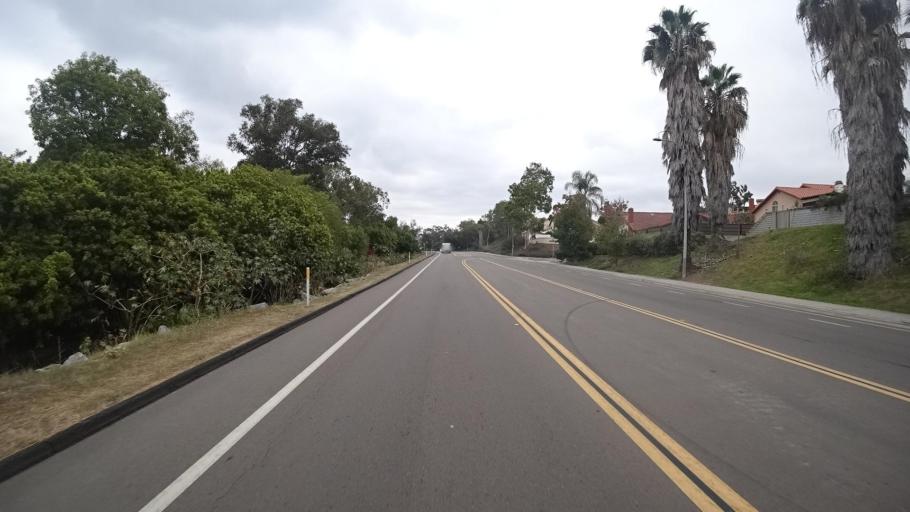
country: US
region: California
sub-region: San Diego County
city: Spring Valley
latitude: 32.7447
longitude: -116.9938
